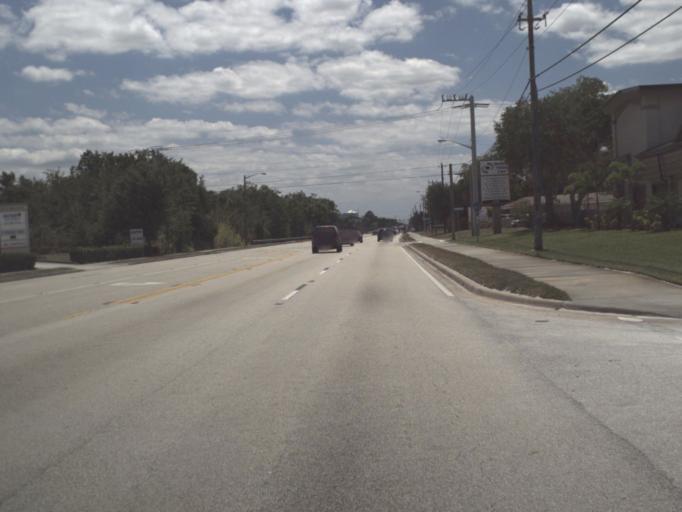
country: US
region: Florida
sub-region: Brevard County
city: Melbourne
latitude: 28.0724
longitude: -80.6214
